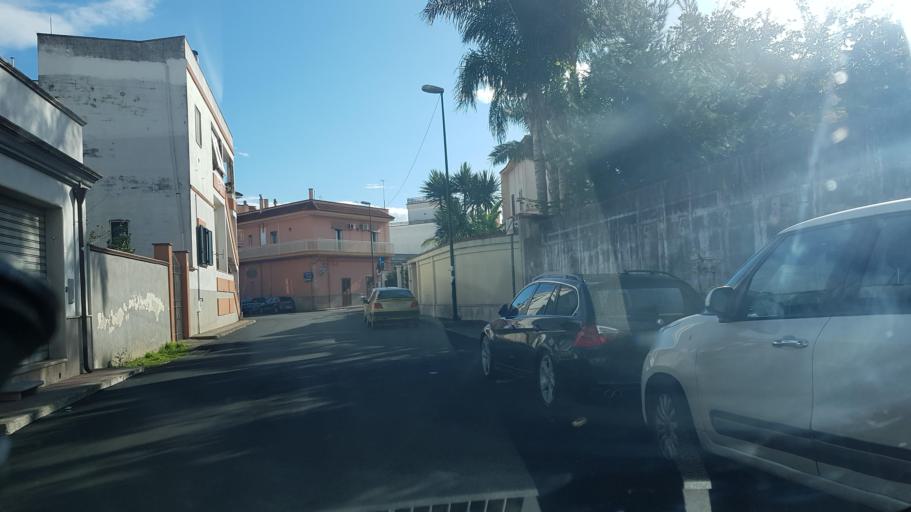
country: IT
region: Apulia
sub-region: Provincia di Brindisi
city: Torre Santa Susanna
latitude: 40.4617
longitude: 17.7389
